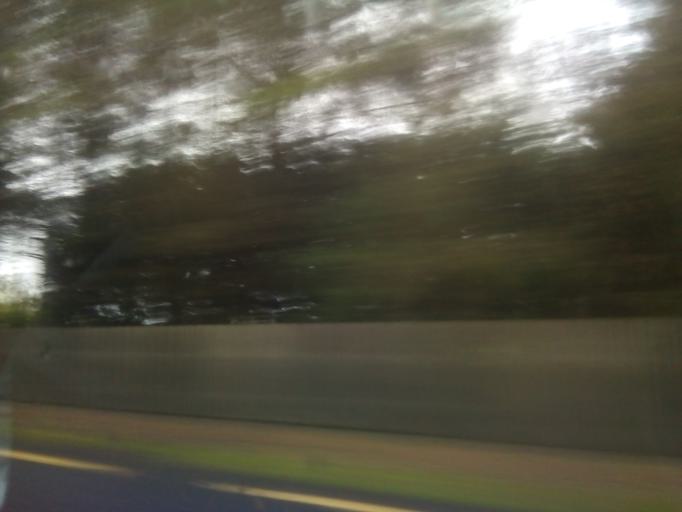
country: IE
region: Connaught
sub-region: Roscommon
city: Boyle
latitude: 53.8026
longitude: -8.3009
